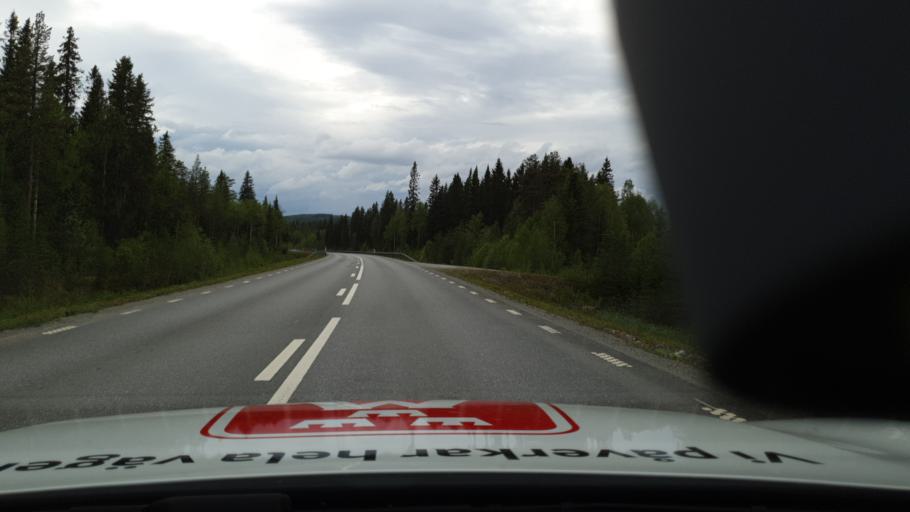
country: SE
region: Vaesterbotten
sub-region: Dorotea Kommun
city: Dorotea
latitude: 64.2871
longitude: 16.5125
